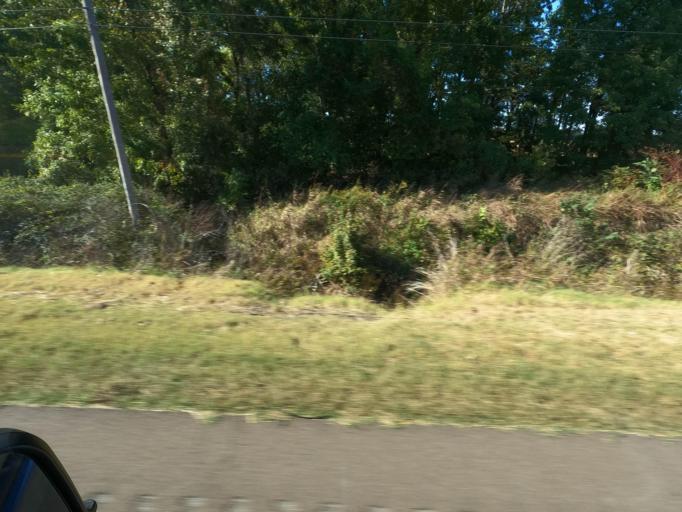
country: US
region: Tennessee
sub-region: Obion County
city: Englewood
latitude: 36.3864
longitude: -89.1060
